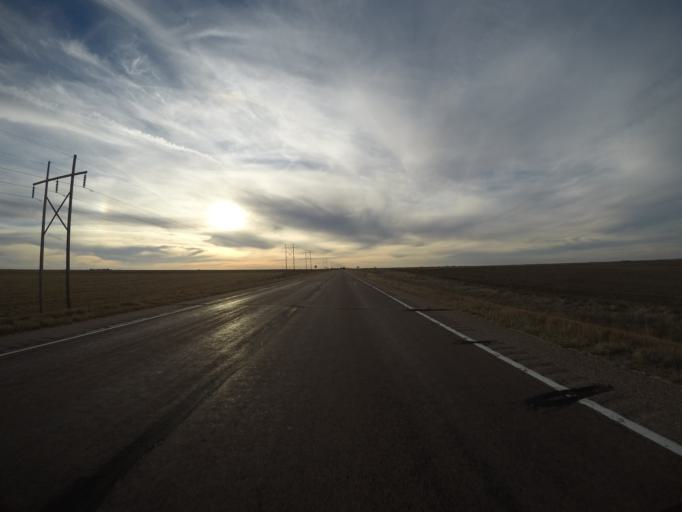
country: US
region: Colorado
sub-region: Yuma County
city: Yuma
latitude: 39.6548
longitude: -102.7996
